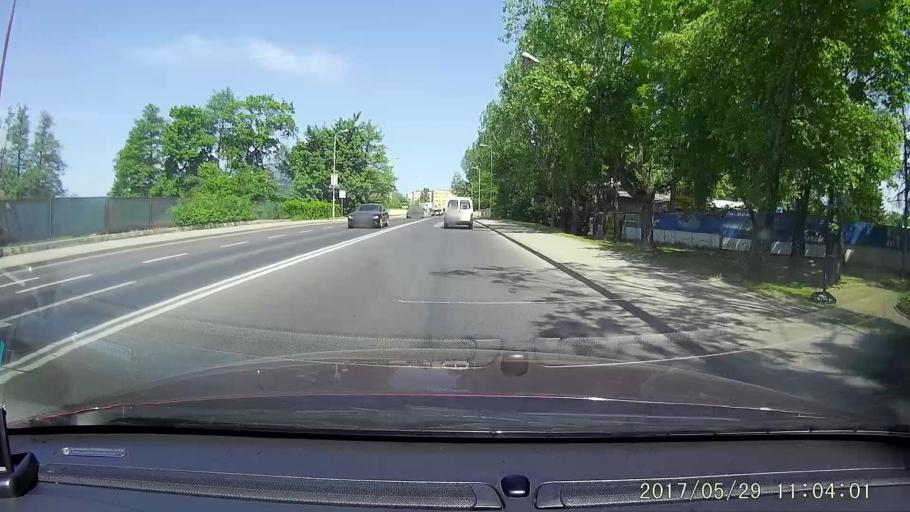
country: PL
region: Lower Silesian Voivodeship
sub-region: Jelenia Gora
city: Jelenia Gora
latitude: 50.9061
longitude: 15.7502
